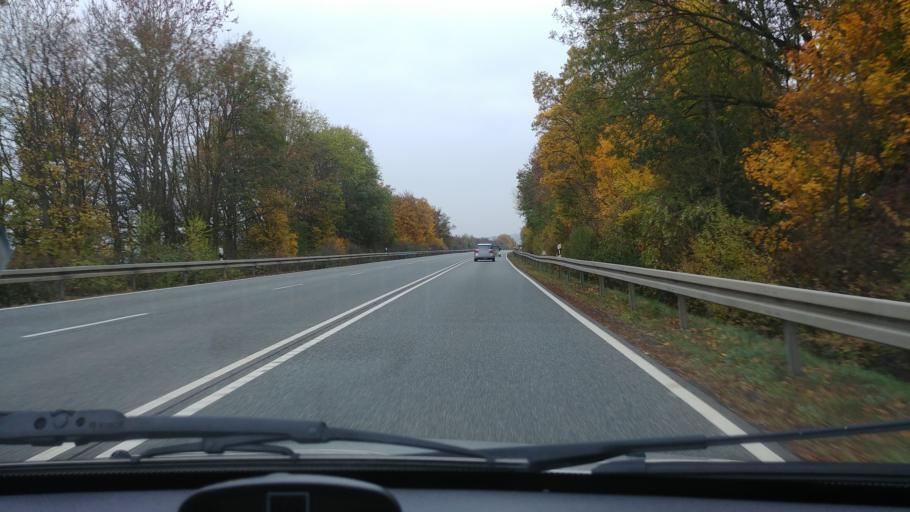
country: DE
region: Hesse
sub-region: Regierungsbezirk Giessen
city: Dehrn
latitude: 50.4478
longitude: 8.0893
